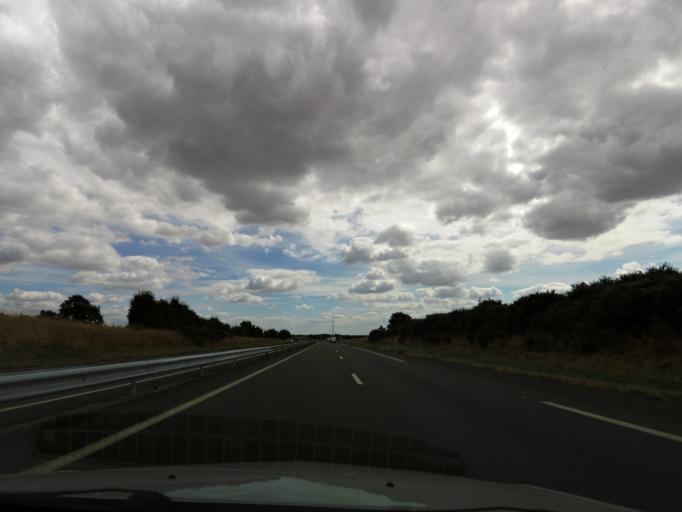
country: FR
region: Pays de la Loire
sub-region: Departement de la Loire-Atlantique
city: La Planche
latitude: 47.0366
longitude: -1.4088
